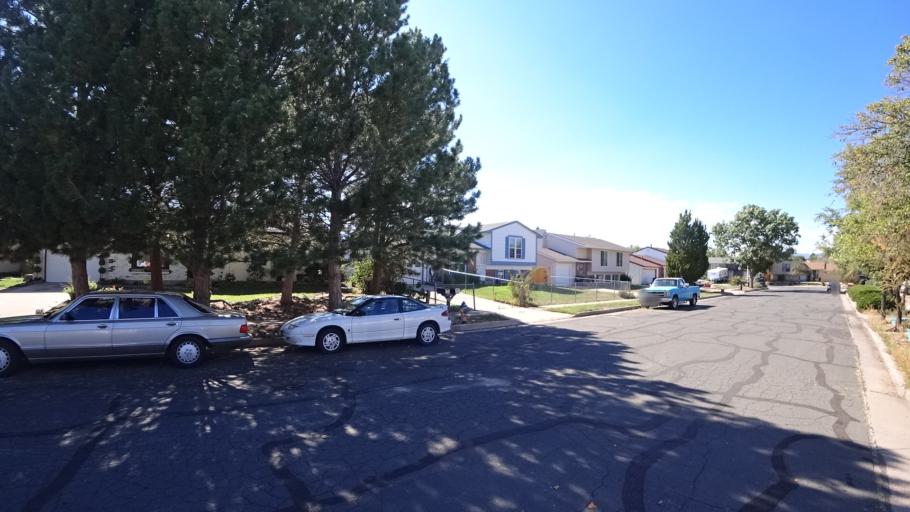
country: US
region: Colorado
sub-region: El Paso County
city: Stratmoor
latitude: 38.7921
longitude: -104.7367
